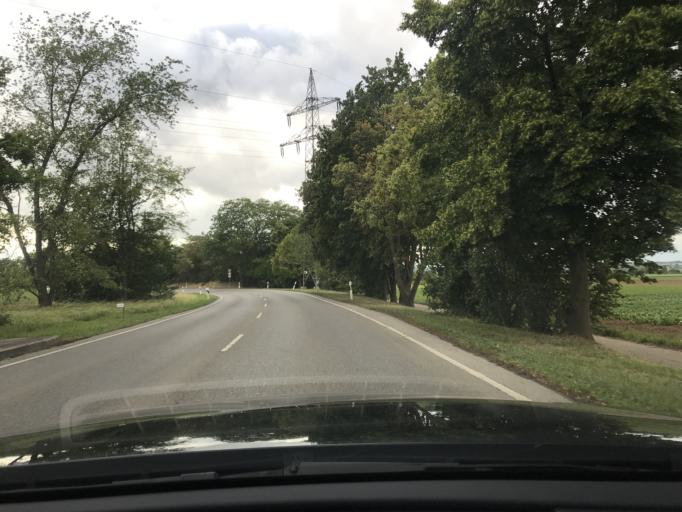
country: DE
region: Baden-Wuerttemberg
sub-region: Regierungsbezirk Stuttgart
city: Stuttgart Muehlhausen
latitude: 48.8339
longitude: 9.2464
